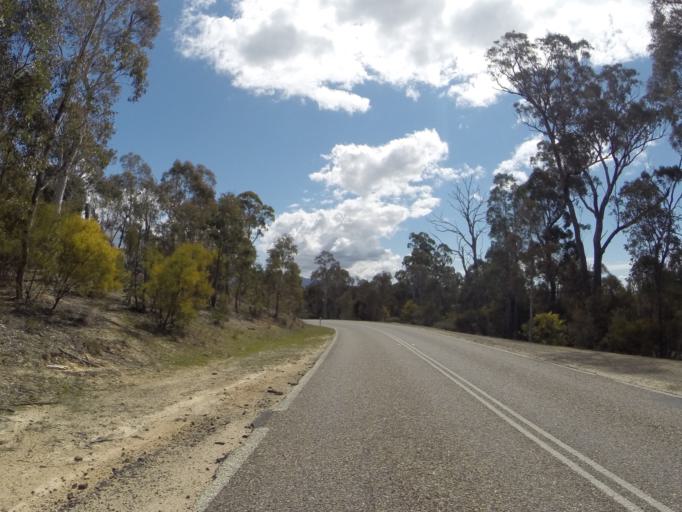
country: AU
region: Australian Capital Territory
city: Macquarie
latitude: -35.3468
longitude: 148.9315
